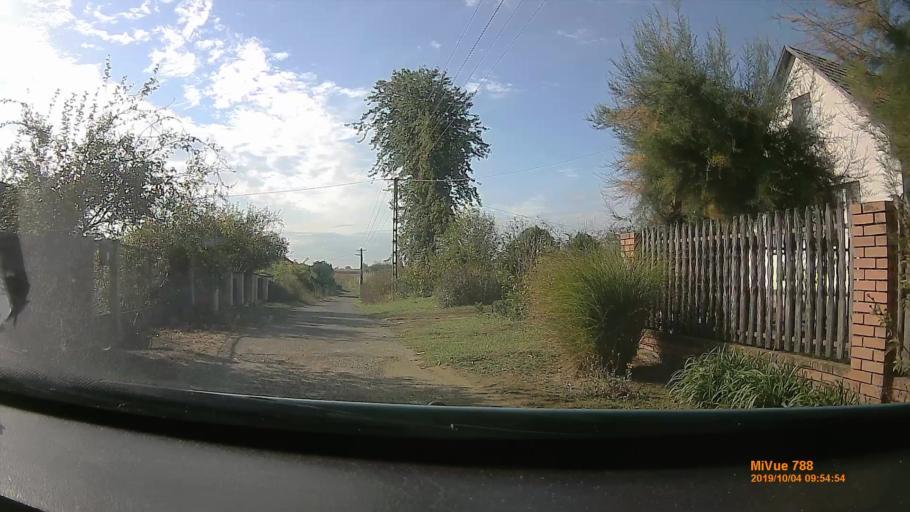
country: HU
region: Szabolcs-Szatmar-Bereg
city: Nyiregyhaza
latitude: 47.9399
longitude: 21.6631
